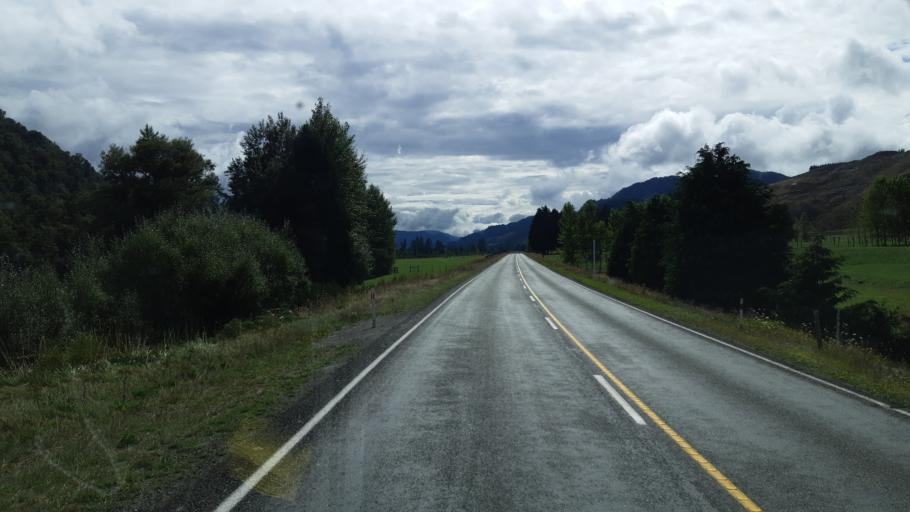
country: NZ
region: West Coast
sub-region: Buller District
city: Westport
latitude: -41.7850
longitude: 172.3701
